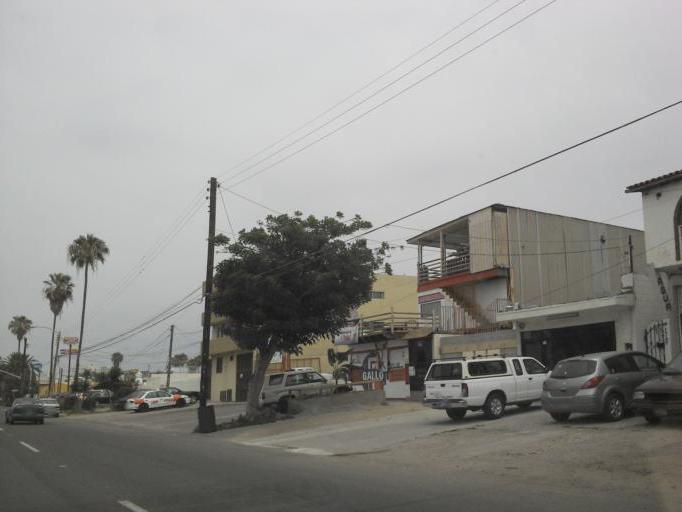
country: US
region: California
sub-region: San Diego County
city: Imperial Beach
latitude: 32.5239
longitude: -117.1200
